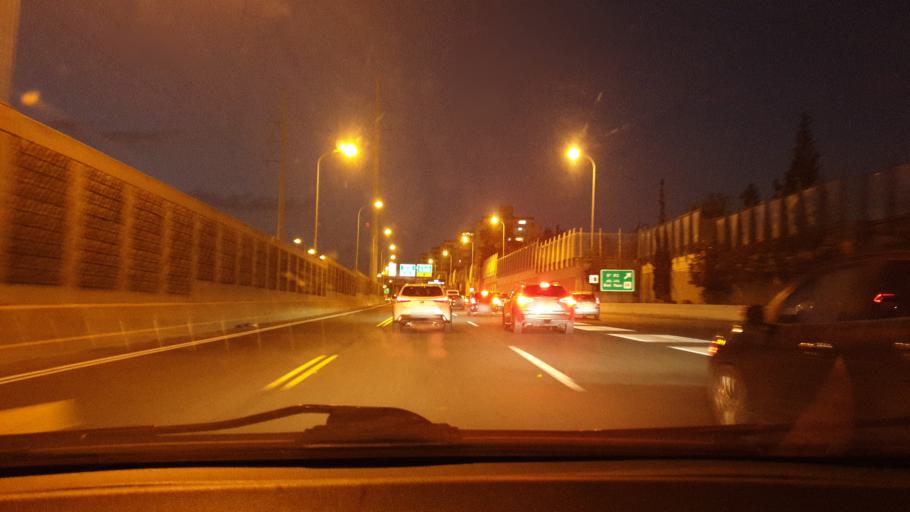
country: IL
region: Tel Aviv
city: Bat Yam
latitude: 32.0171
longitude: 34.7622
